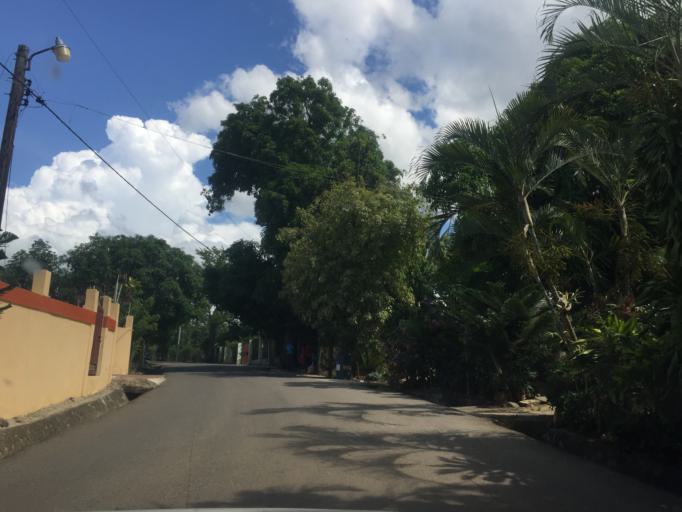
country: DO
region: La Vega
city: Rio Verde Arriba
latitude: 19.3612
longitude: -70.5983
